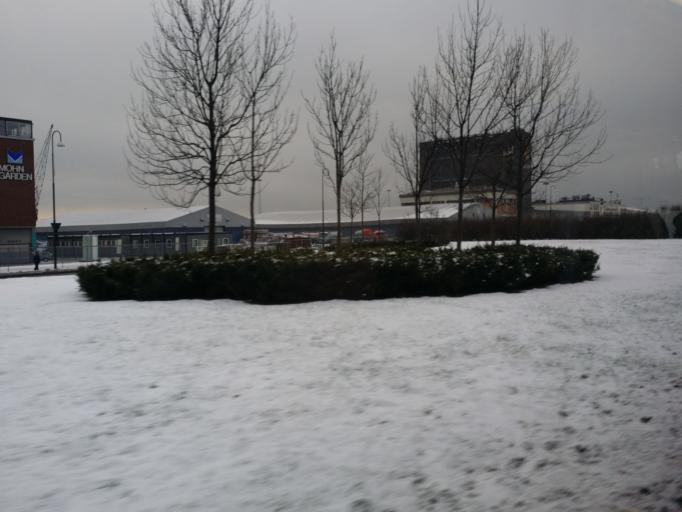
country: NO
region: Oslo
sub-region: Oslo
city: Oslo
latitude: 59.9104
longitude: 10.7187
